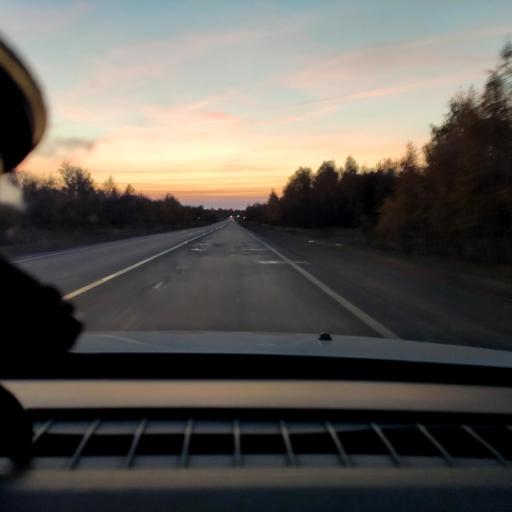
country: RU
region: Samara
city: Chapayevsk
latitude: 52.9933
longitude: 49.8250
